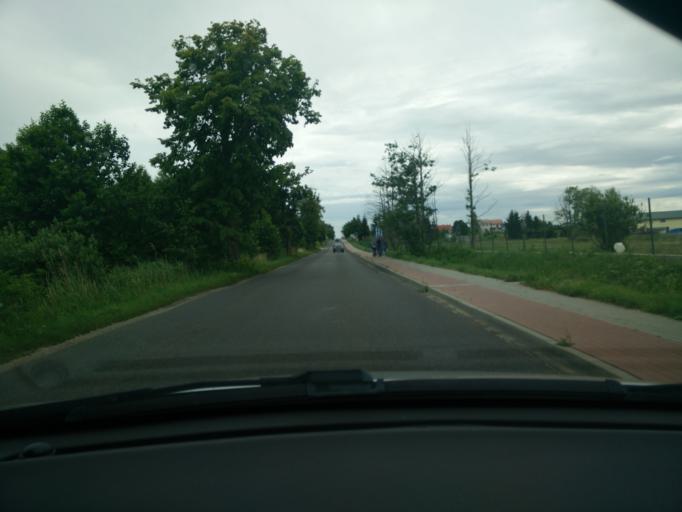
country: PL
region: Pomeranian Voivodeship
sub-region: Powiat pucki
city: Mosty
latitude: 54.6240
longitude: 18.4965
